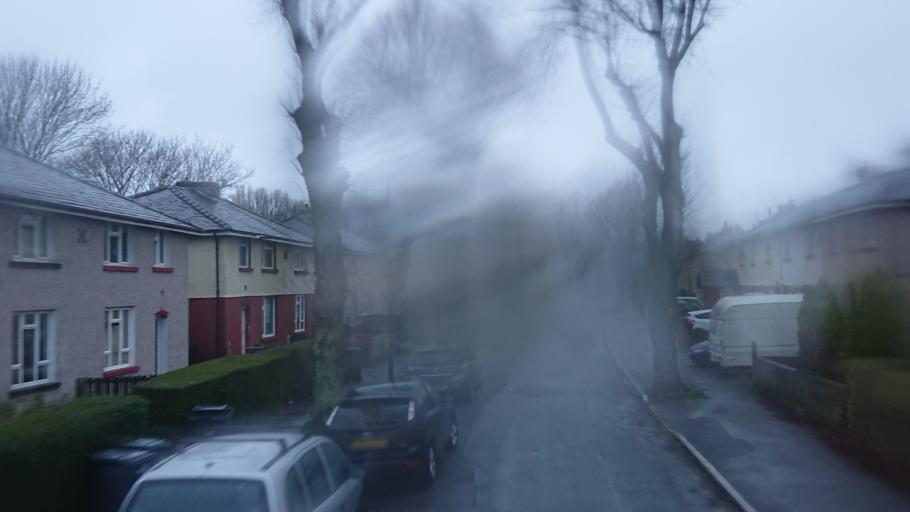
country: GB
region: England
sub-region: Lancashire
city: Lancaster
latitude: 54.0587
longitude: -2.7894
